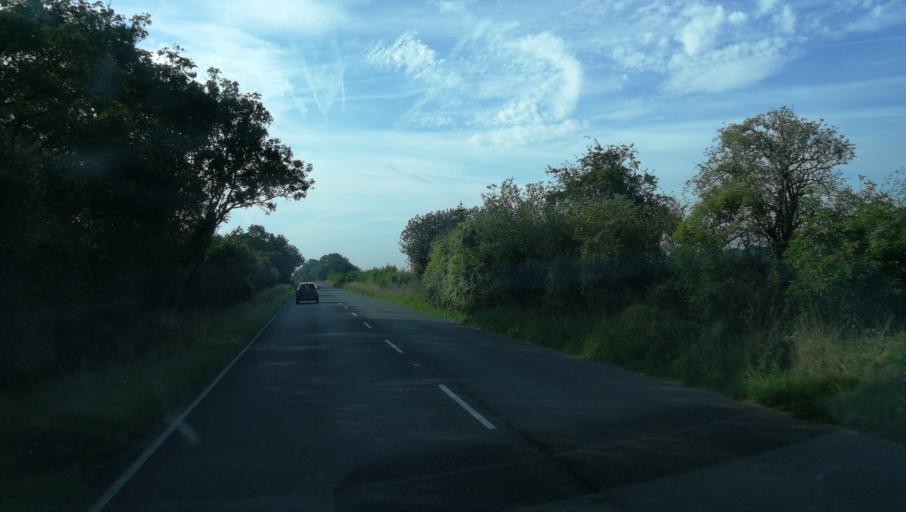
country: GB
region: England
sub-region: Oxfordshire
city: Woodstock
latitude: 51.8662
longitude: -1.3262
